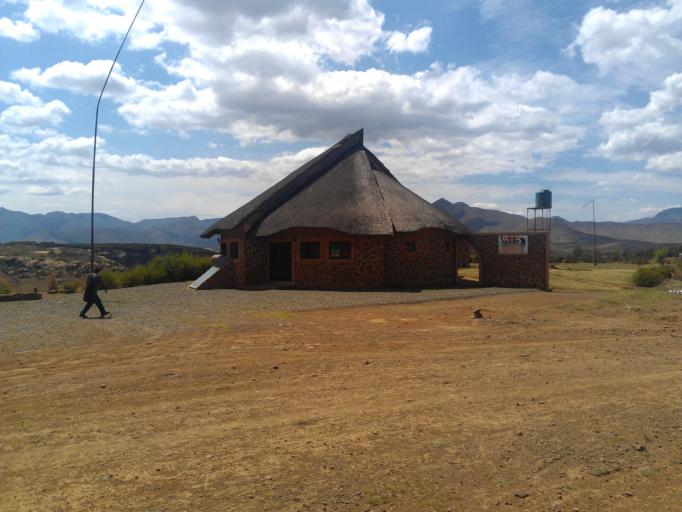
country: LS
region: Berea
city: Teyateyaneng
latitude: -29.2444
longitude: 27.8667
